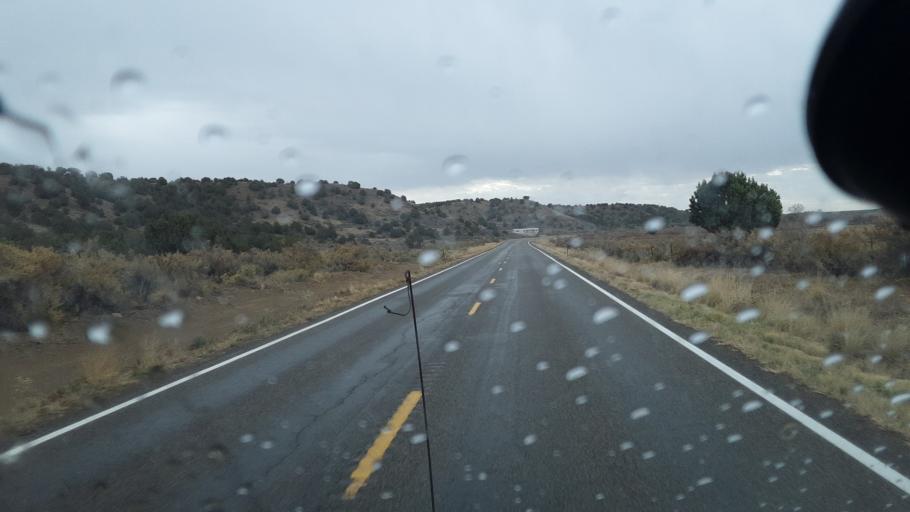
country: US
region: New Mexico
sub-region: San Juan County
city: Spencerville
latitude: 37.0106
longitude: -108.1820
